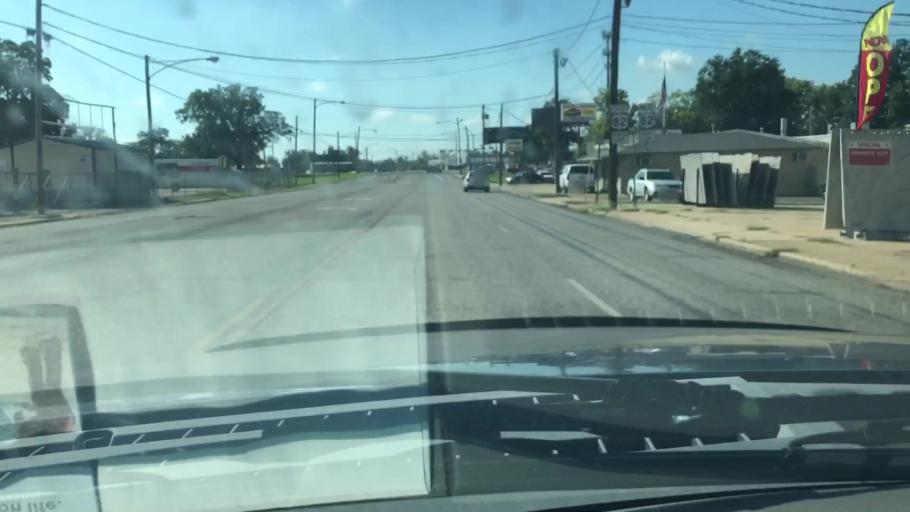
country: US
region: Texas
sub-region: Bowie County
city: Texarkana
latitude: 33.4369
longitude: -94.0532
